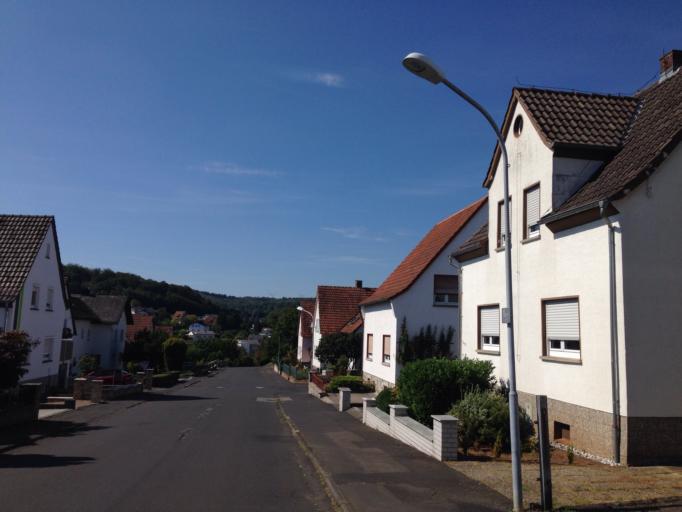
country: DE
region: Hesse
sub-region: Regierungsbezirk Giessen
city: Heuchelheim
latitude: 50.6248
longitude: 8.5882
